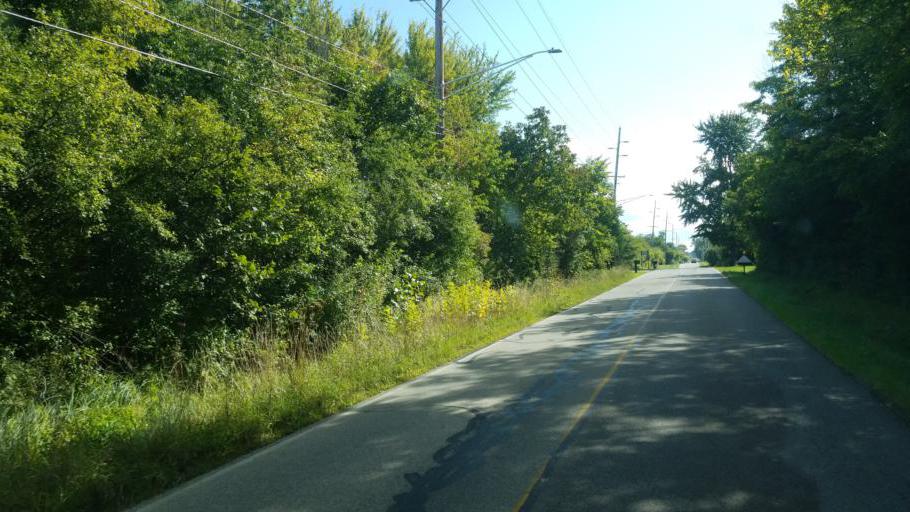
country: US
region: Ohio
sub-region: Lorain County
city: Oberlin
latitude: 41.2795
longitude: -82.2091
